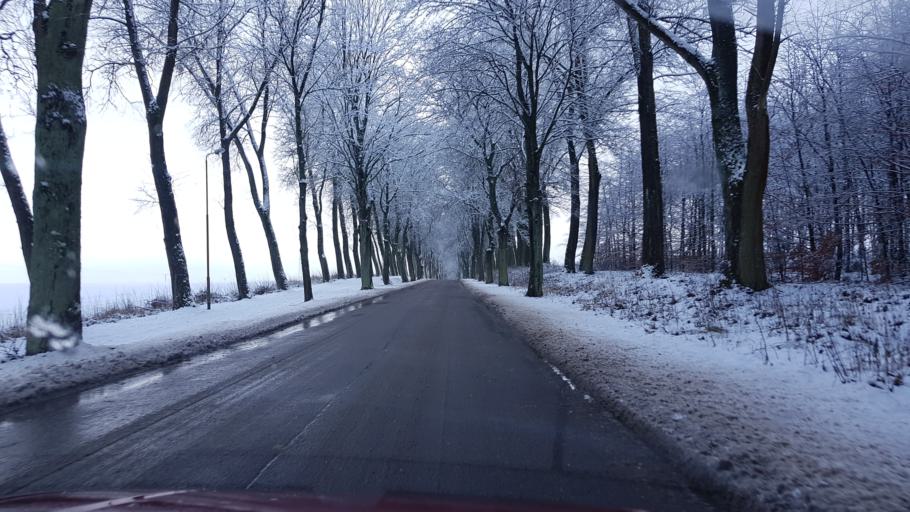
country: PL
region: West Pomeranian Voivodeship
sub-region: Powiat drawski
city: Zlocieniec
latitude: 53.5400
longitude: 16.0461
